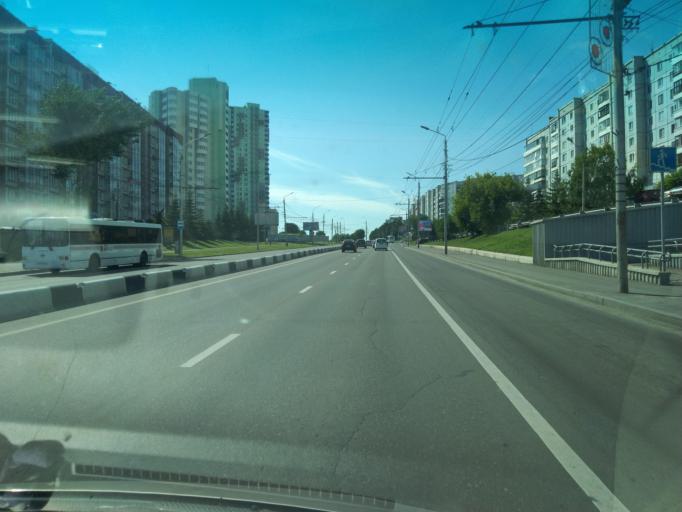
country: RU
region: Krasnoyarskiy
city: Krasnoyarsk
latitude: 56.0126
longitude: 92.8249
